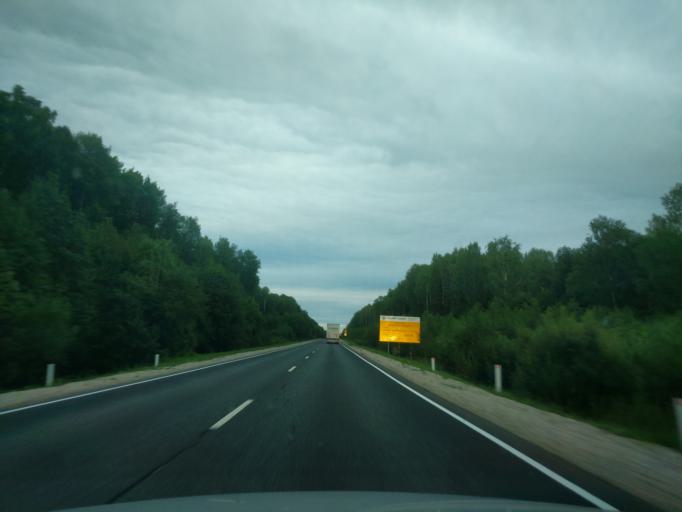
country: RU
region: Kostroma
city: Ponazyrevo
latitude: 58.3233
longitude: 46.5268
